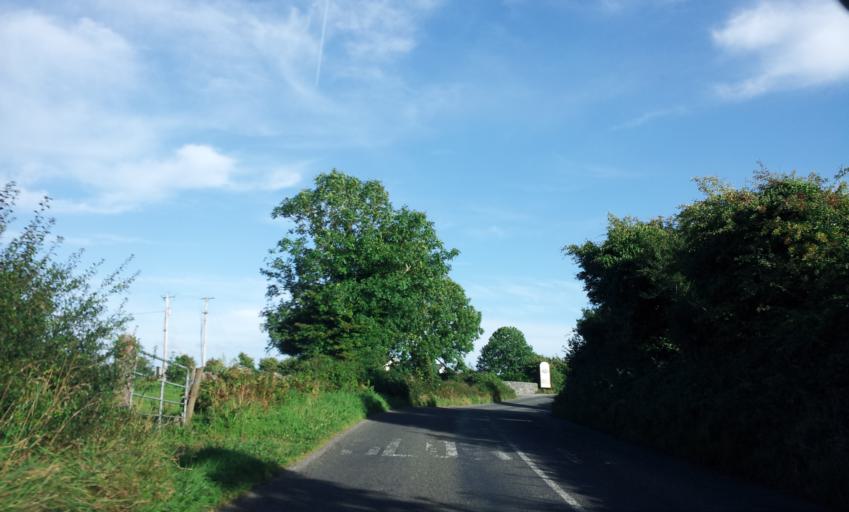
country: IE
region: Munster
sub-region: An Clar
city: Ennis
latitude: 52.9520
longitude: -9.0691
